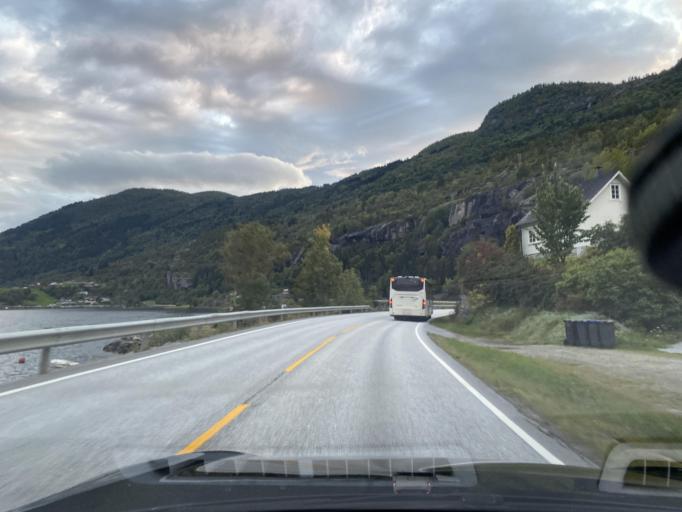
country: NO
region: Sogn og Fjordane
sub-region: Sogndal
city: Sogndalsfjora
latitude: 61.2593
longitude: 7.1512
